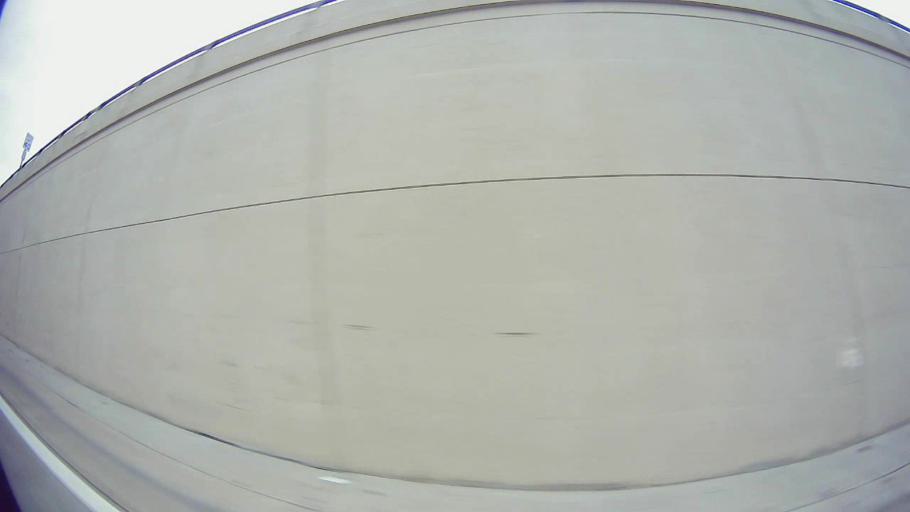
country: US
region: Michigan
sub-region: Oakland County
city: Southfield
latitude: 42.4513
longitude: -83.2109
